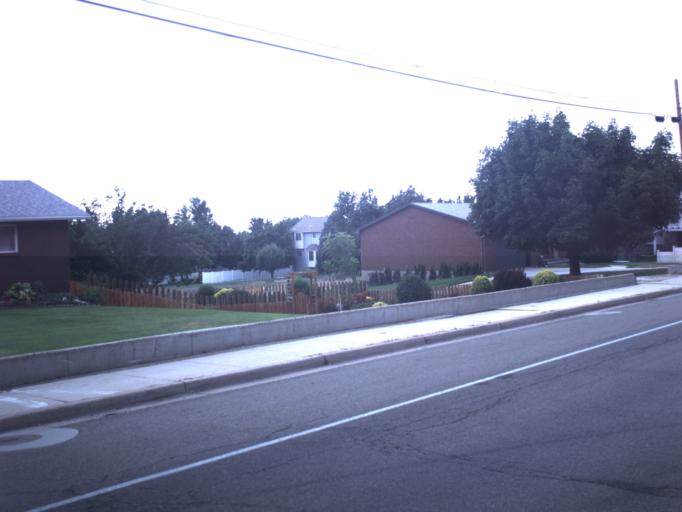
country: US
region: Utah
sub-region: Davis County
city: Centerville
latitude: 40.9438
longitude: -111.8806
